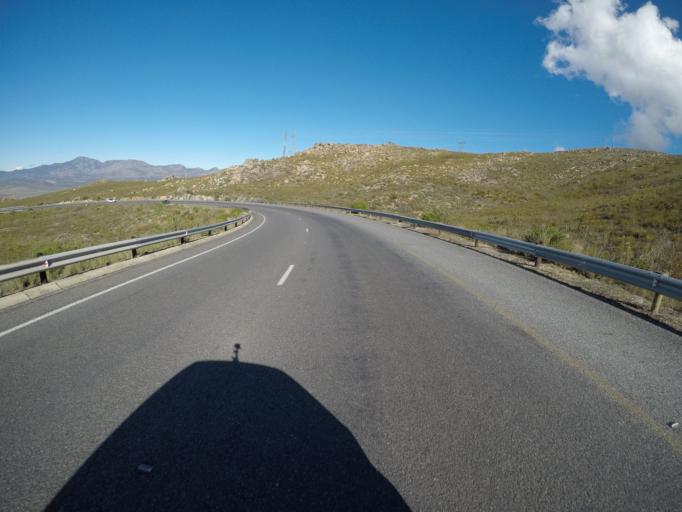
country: ZA
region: Western Cape
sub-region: Overberg District Municipality
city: Grabouw
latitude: -34.2229
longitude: 19.1719
